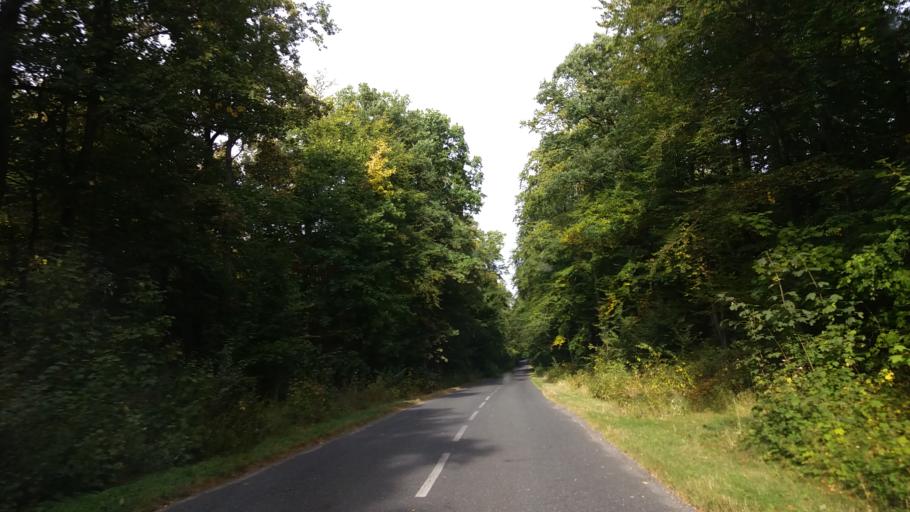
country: PL
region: West Pomeranian Voivodeship
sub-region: Powiat choszczenski
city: Krzecin
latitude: 53.0156
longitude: 15.5058
